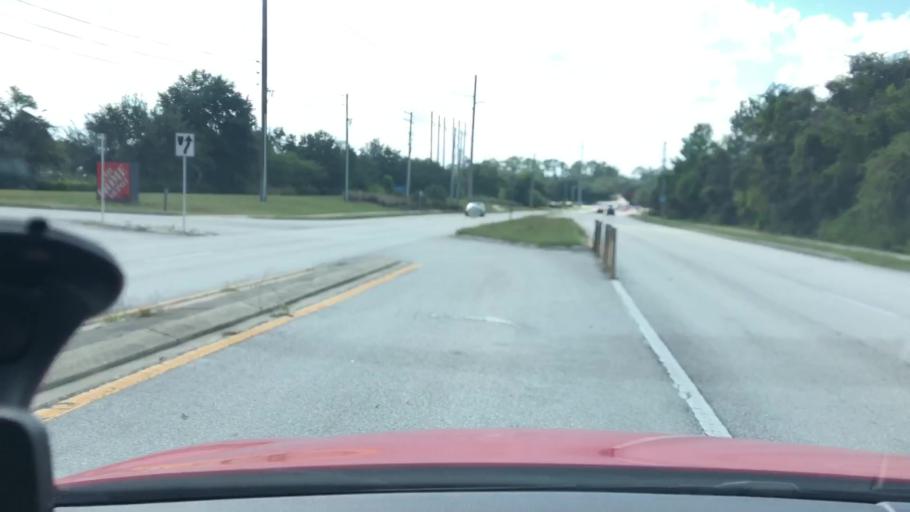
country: US
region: Florida
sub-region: Volusia County
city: Deltona
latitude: 28.9149
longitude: -81.2817
